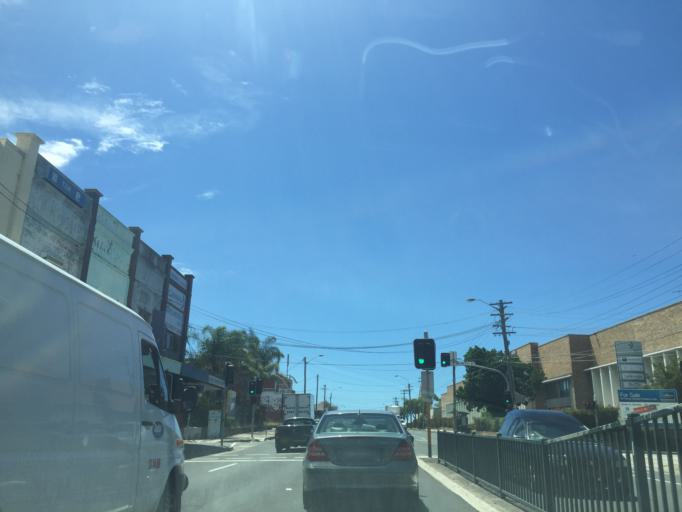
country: AU
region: New South Wales
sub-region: Rockdale
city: Arncliffe
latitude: -33.9236
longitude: 151.1620
